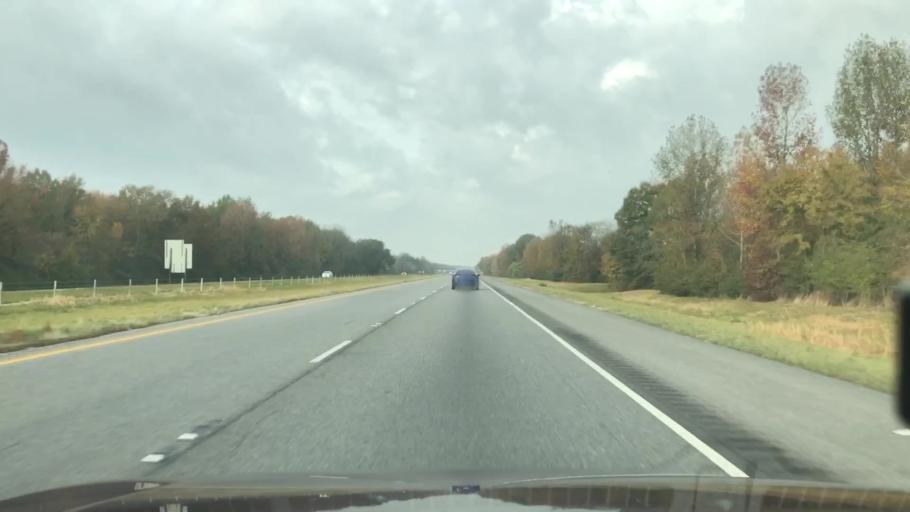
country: US
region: Louisiana
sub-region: Richland Parish
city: Delhi
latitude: 32.4452
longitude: -91.5129
